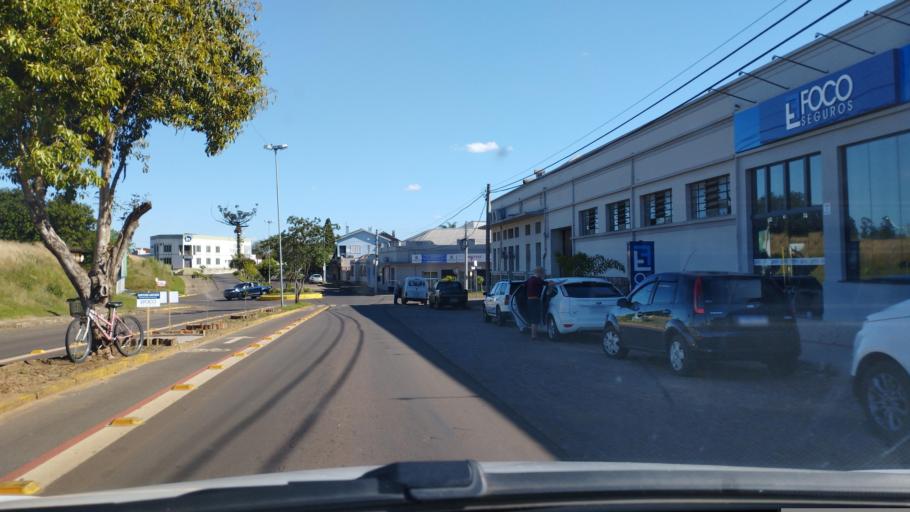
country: BR
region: Rio Grande do Sul
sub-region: Tupancireta
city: Tupancireta
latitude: -29.0848
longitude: -53.8346
